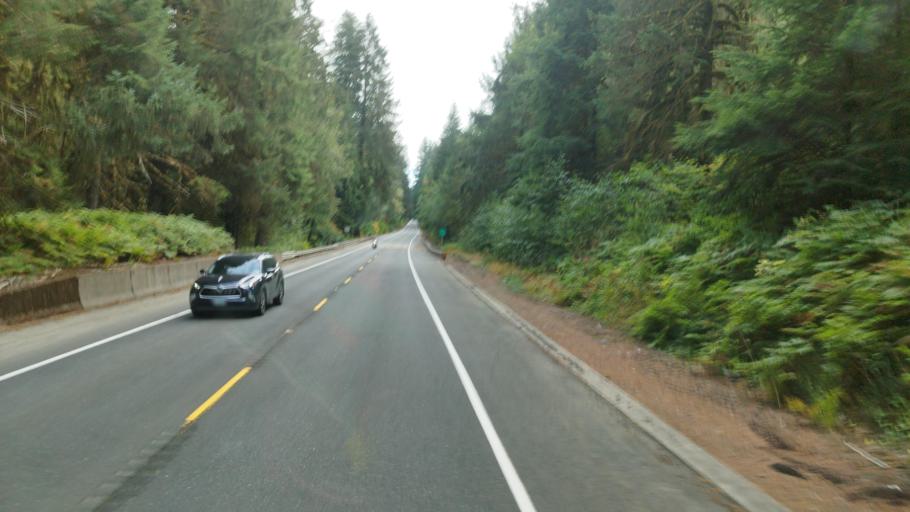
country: US
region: Oregon
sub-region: Clatsop County
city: Seaside
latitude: 45.8944
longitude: -123.6434
